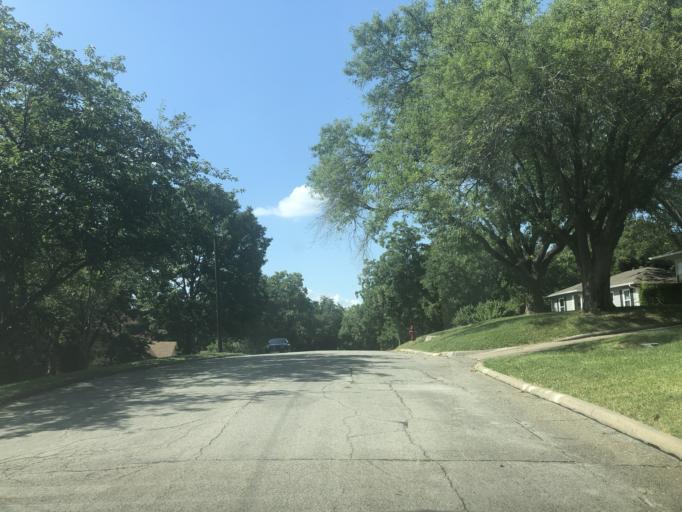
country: US
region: Texas
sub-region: Dallas County
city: Grand Prairie
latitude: 32.7548
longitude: -97.0004
